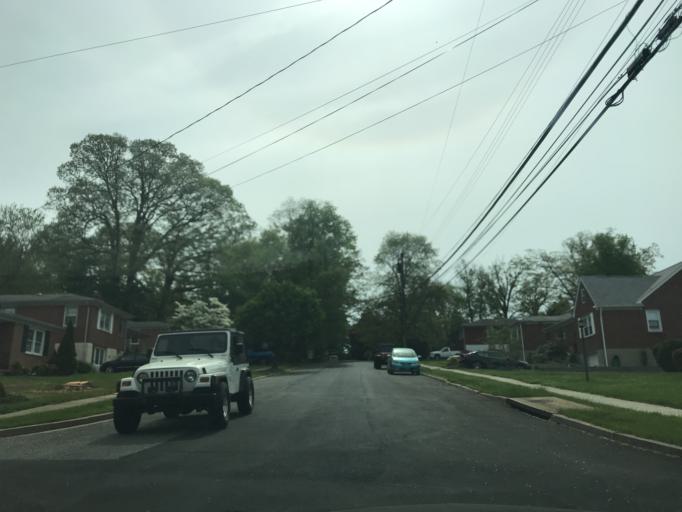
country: US
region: Maryland
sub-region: Howard County
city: Ilchester
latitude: 39.2761
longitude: -76.7580
